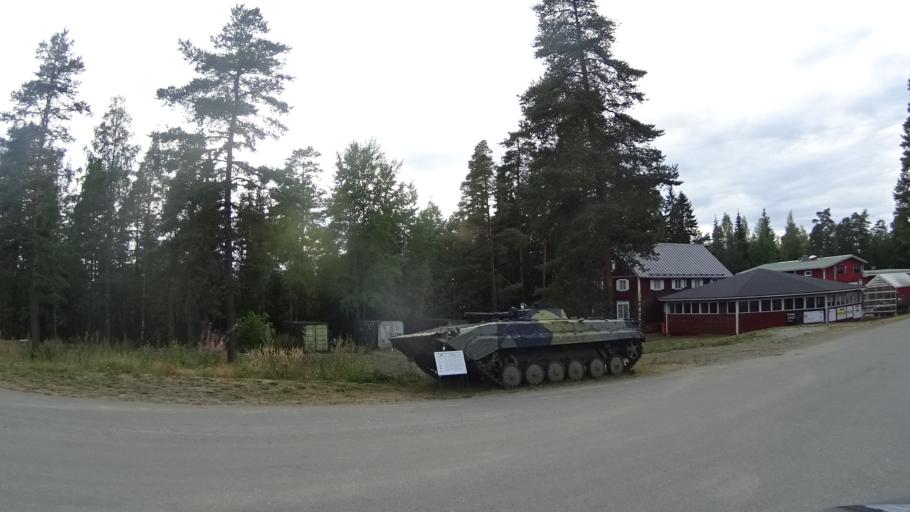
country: FI
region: Haeme
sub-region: Haemeenlinna
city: Parola
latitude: 61.0415
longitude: 24.3457
